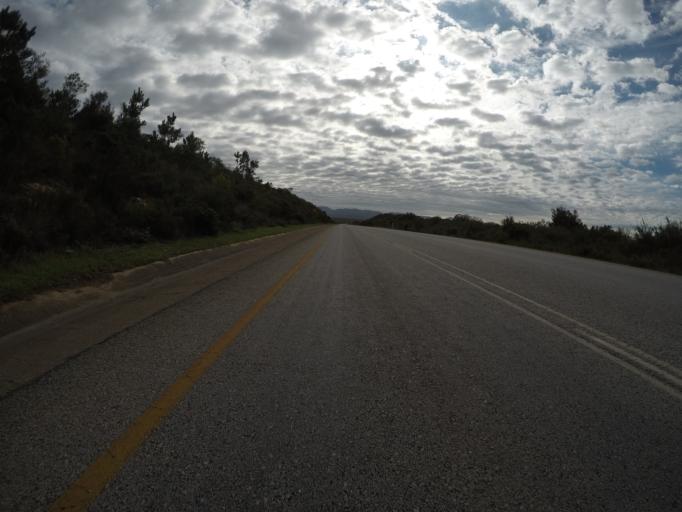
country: ZA
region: Eastern Cape
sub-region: Cacadu District Municipality
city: Kruisfontein
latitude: -34.0387
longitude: 24.5490
